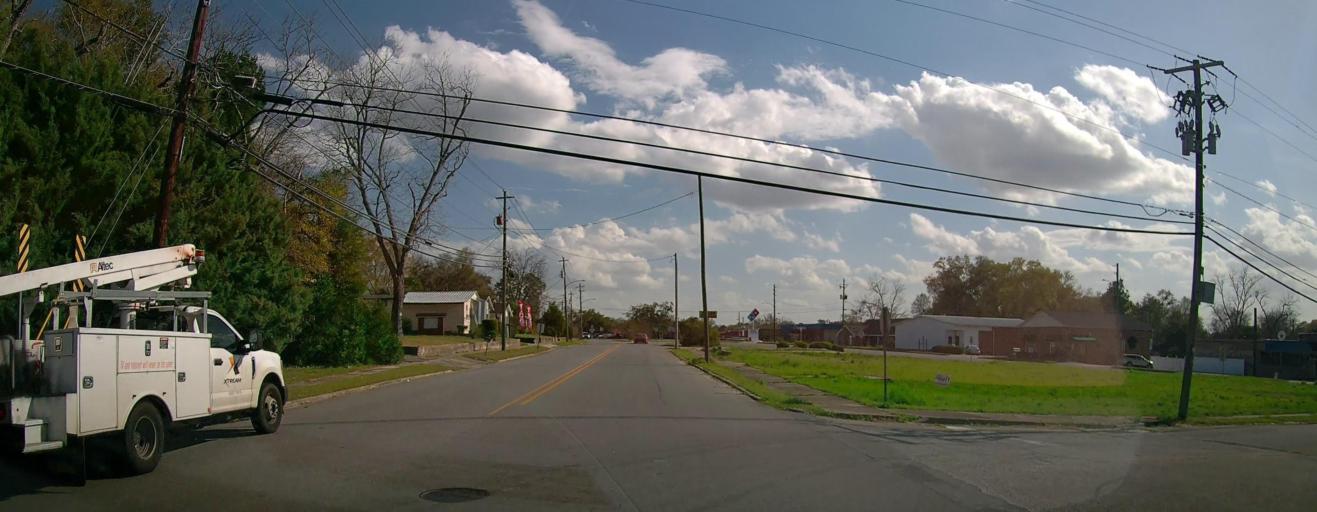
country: US
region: Georgia
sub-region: Dodge County
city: Eastman
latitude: 32.1932
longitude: -83.1747
